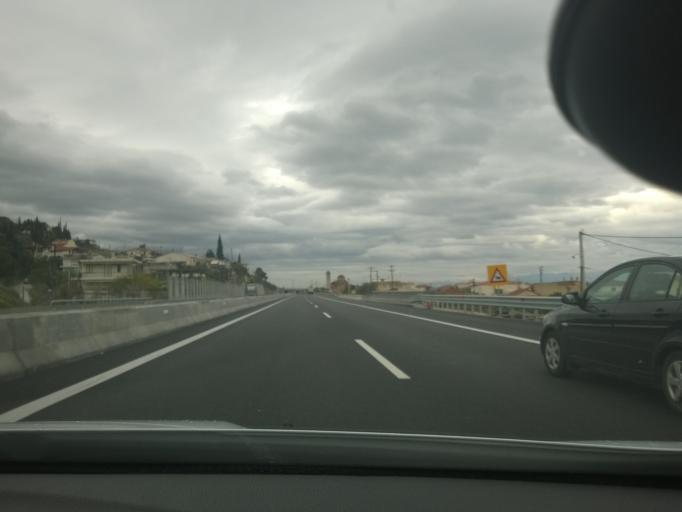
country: GR
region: Peloponnese
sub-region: Nomos Korinthias
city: Kato Dhiminio
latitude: 38.0465
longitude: 22.6918
